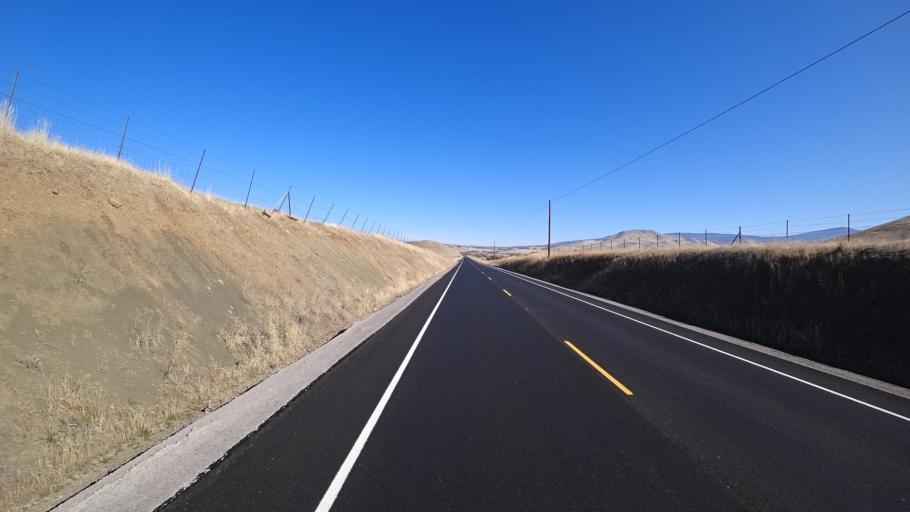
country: US
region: California
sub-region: Siskiyou County
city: Montague
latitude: 41.8313
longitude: -122.4903
